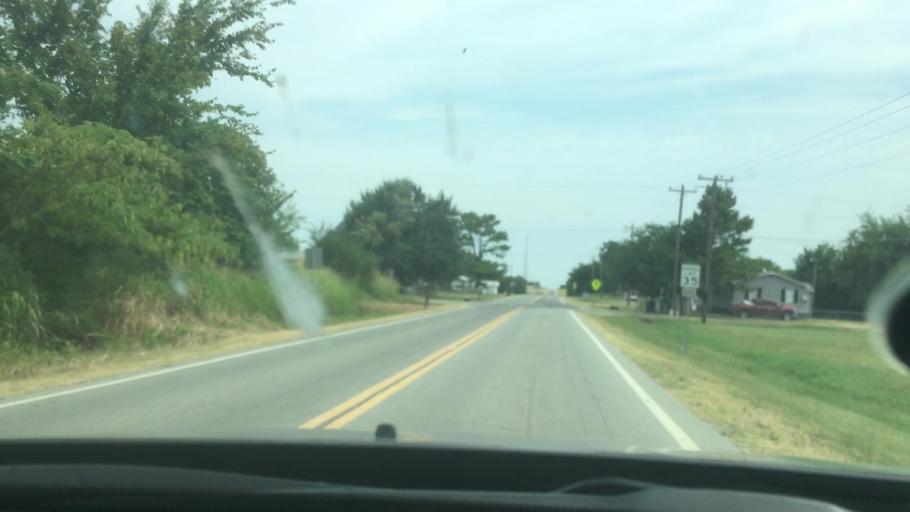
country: US
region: Oklahoma
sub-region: Coal County
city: Coalgate
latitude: 34.5999
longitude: -96.4244
